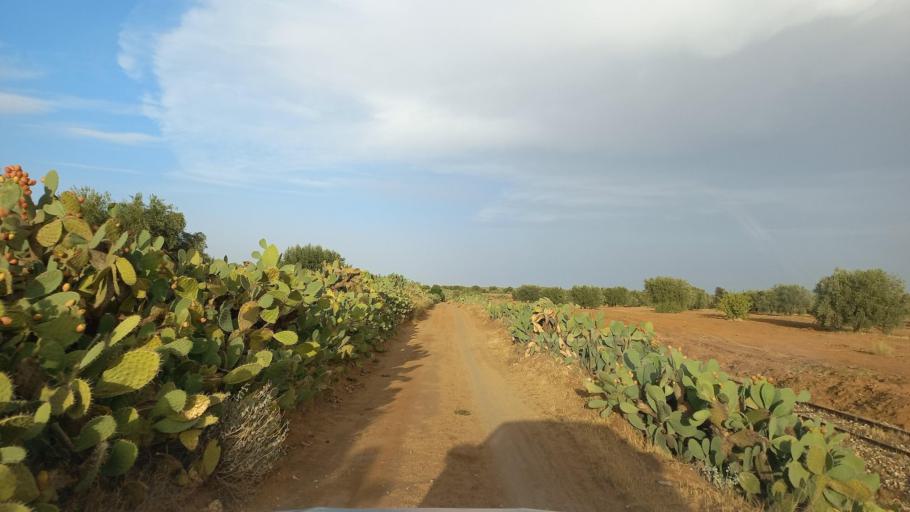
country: TN
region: Al Qasrayn
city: Kasserine
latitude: 35.2247
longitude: 9.0616
